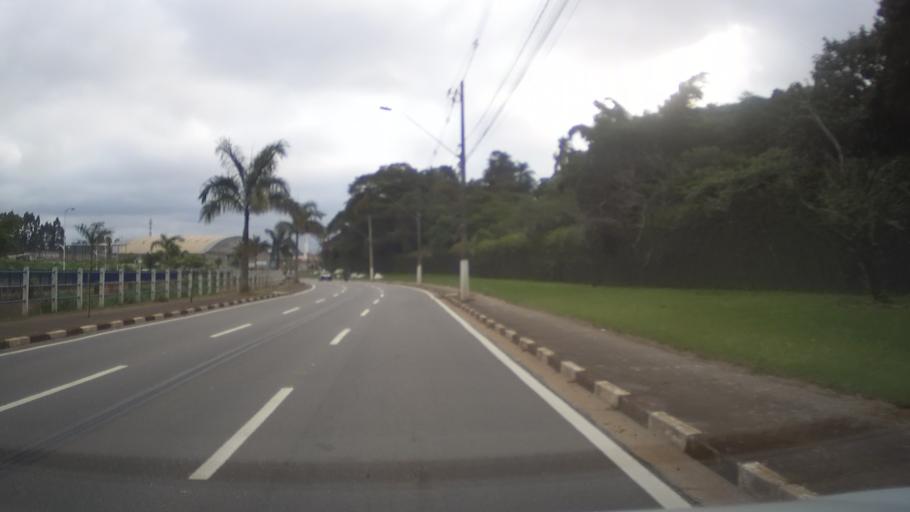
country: BR
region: Sao Paulo
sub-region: Aruja
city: Aruja
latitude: -23.4121
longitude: -46.3689
